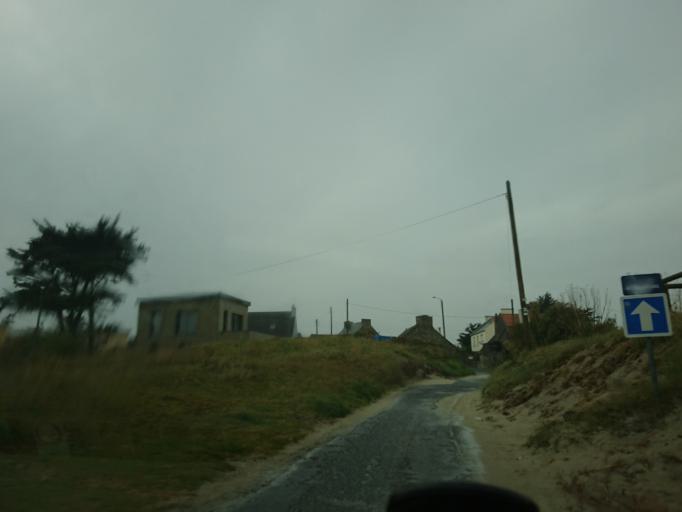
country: FR
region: Brittany
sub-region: Departement du Finistere
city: Guisseny
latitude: 48.6377
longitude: -4.4401
